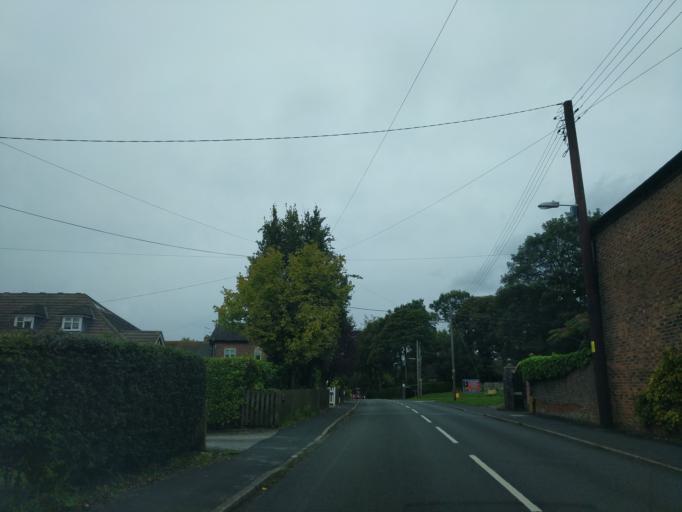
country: GB
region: England
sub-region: Cheshire East
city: Chorlton
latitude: 53.0360
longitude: -2.3688
